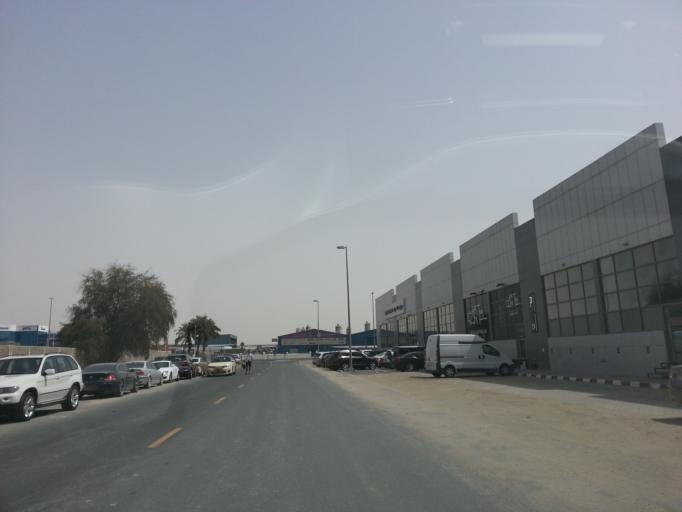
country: AE
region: Dubai
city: Dubai
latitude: 25.1426
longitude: 55.2264
